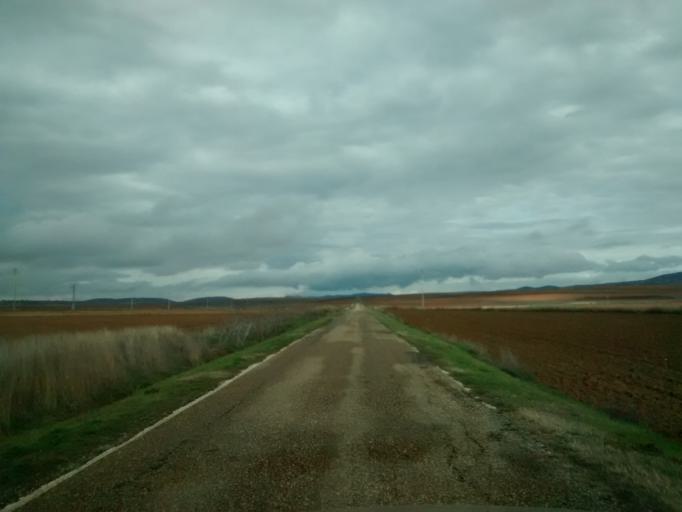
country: ES
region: Aragon
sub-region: Provincia de Zaragoza
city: Torralba de los Frailes
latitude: 41.0466
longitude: -1.6124
